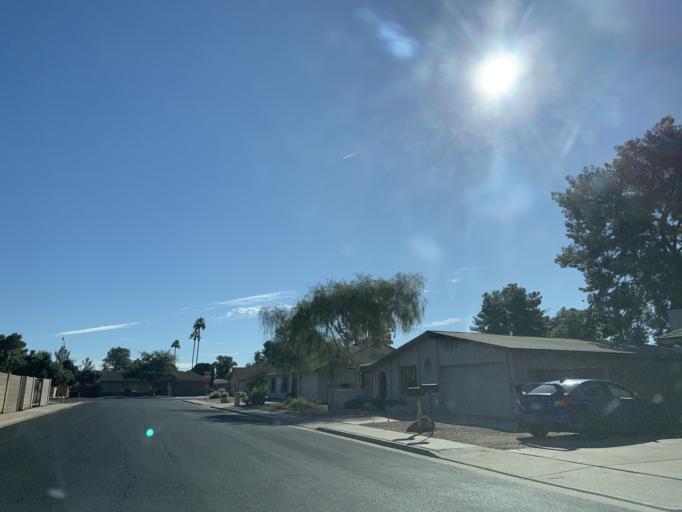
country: US
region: Arizona
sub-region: Maricopa County
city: San Carlos
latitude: 33.3677
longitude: -111.8631
